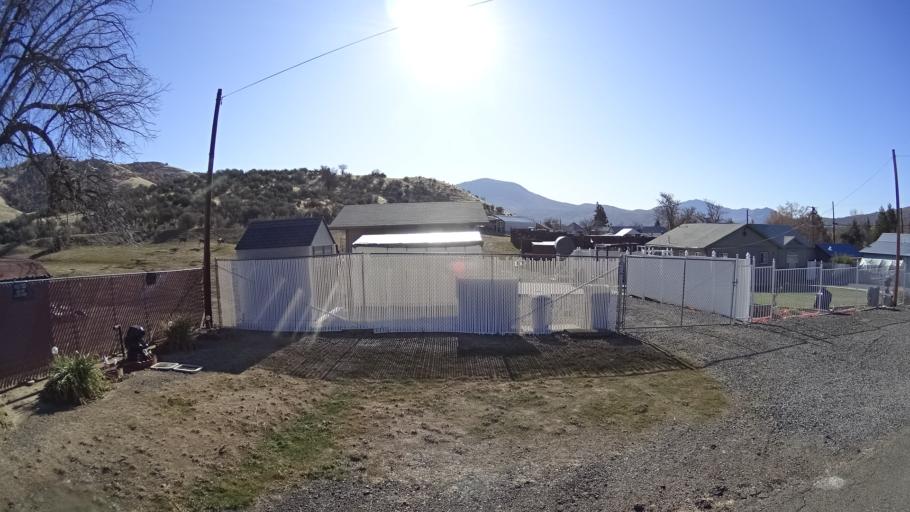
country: US
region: California
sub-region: Siskiyou County
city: Montague
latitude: 41.9126
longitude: -122.5553
